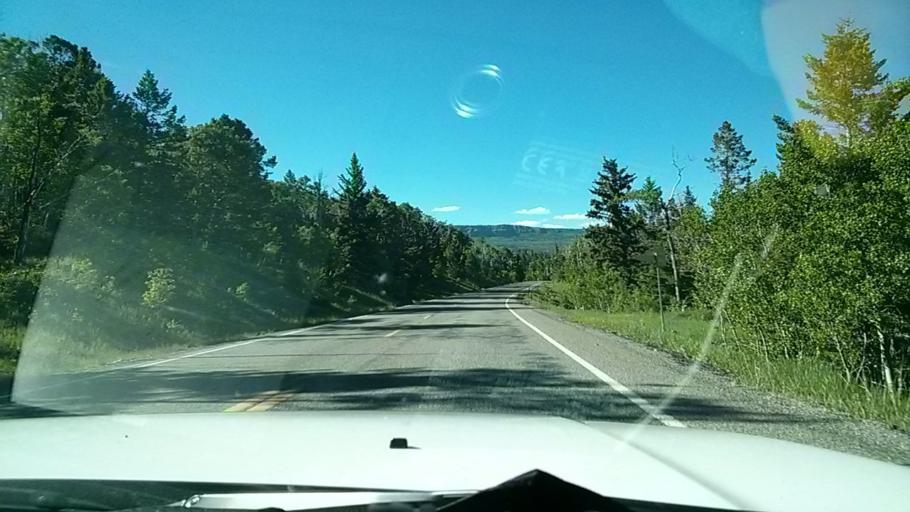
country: US
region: Utah
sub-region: Wayne County
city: Loa
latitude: 38.0754
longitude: -111.3385
